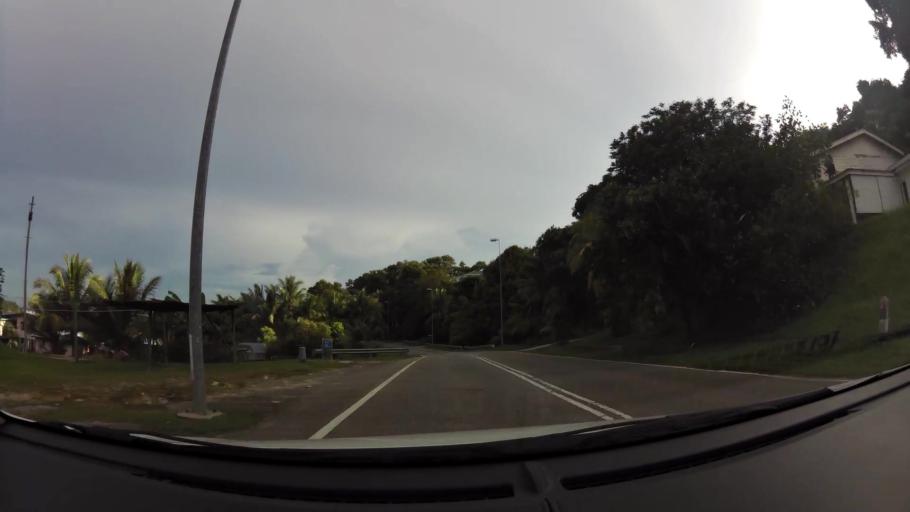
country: BN
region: Brunei and Muara
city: Bandar Seri Begawan
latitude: 4.9372
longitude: 115.0180
